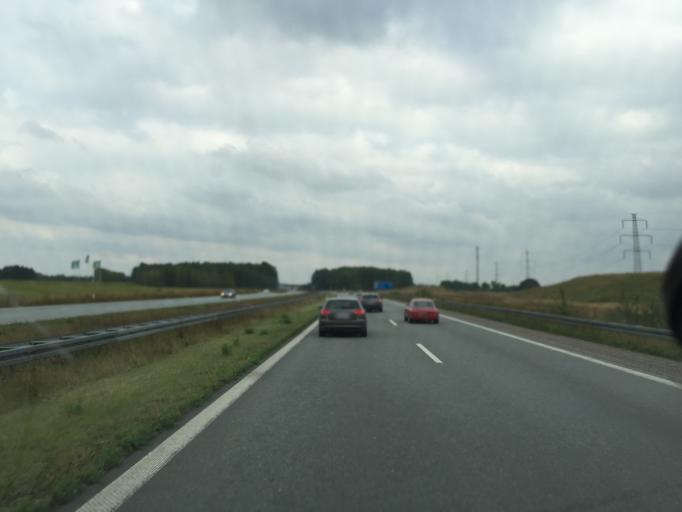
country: DK
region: Zealand
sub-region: Ringsted Kommune
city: Ringsted
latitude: 55.4546
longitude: 11.8148
